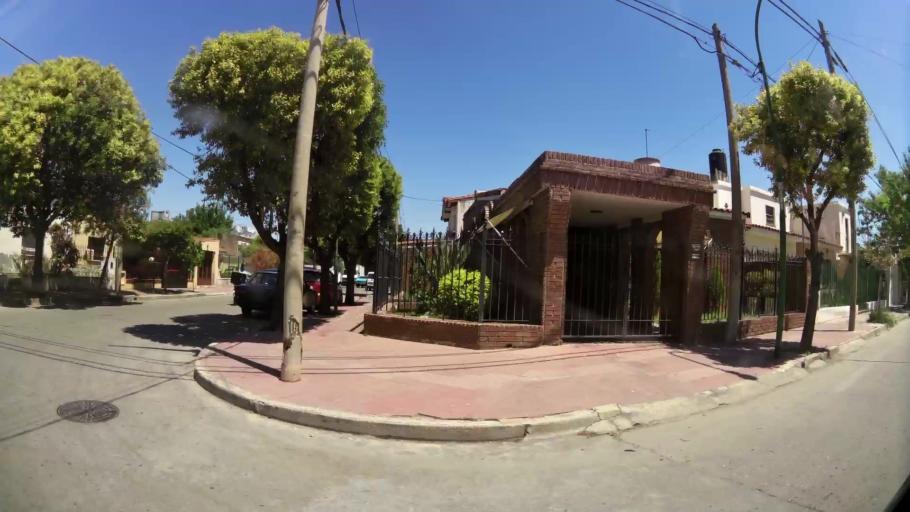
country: AR
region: Cordoba
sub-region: Departamento de Capital
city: Cordoba
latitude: -31.3899
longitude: -64.1420
